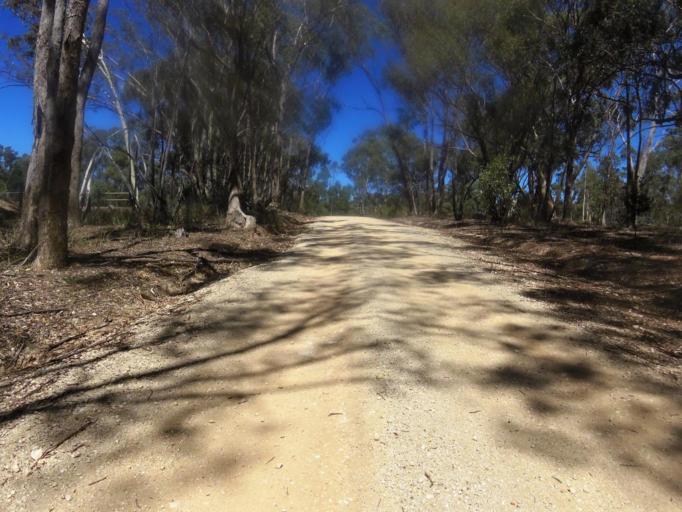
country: AU
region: Victoria
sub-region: Mount Alexander
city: Castlemaine
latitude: -37.0498
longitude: 144.1822
